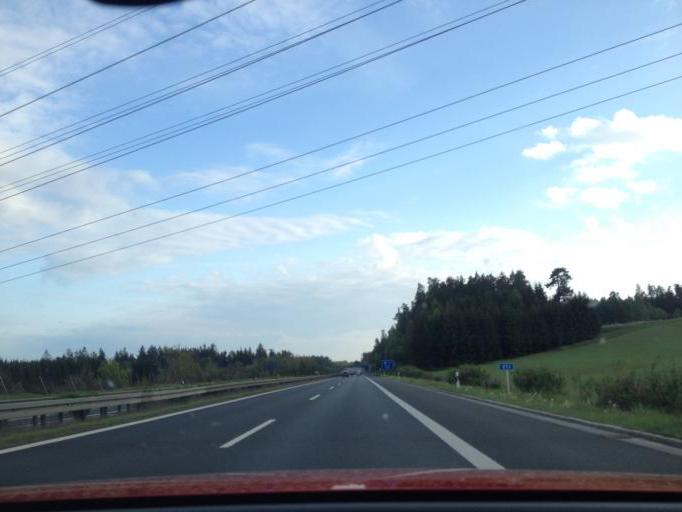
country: DE
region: Bavaria
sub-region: Upper Palatinate
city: Mitterteich
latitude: 49.9252
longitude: 12.2250
